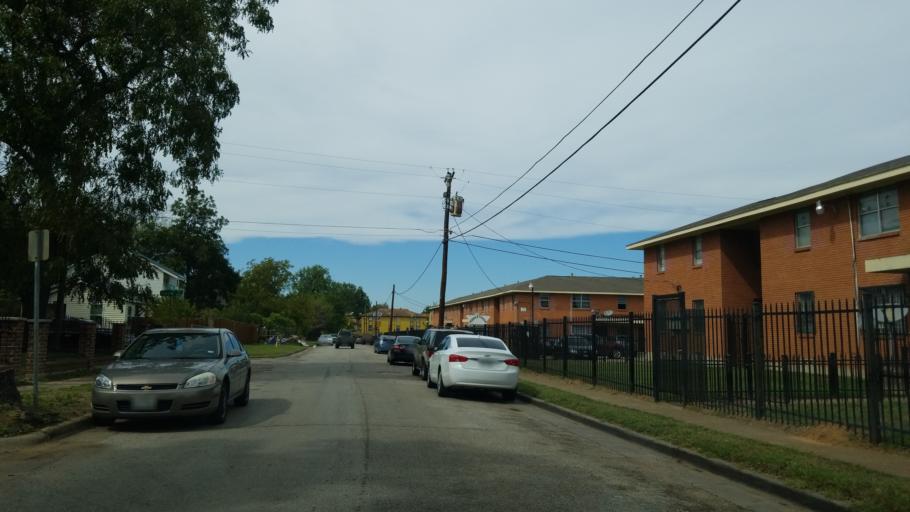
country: US
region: Texas
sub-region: Dallas County
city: Dallas
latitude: 32.7691
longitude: -96.7394
